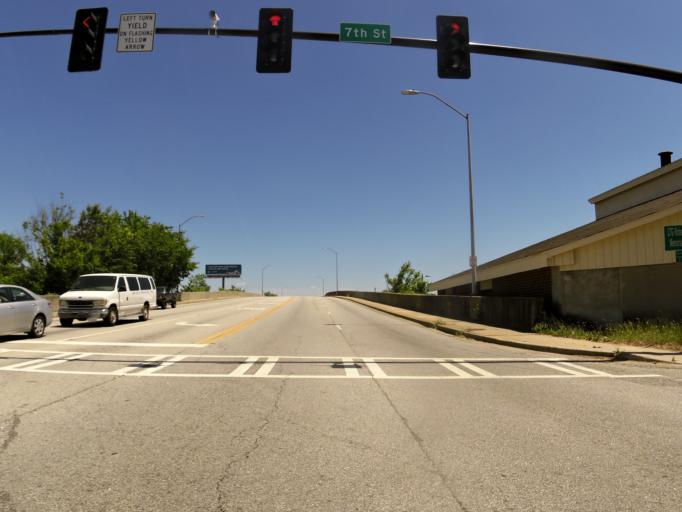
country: US
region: Georgia
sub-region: Richmond County
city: Augusta
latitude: 33.4674
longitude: -81.9669
